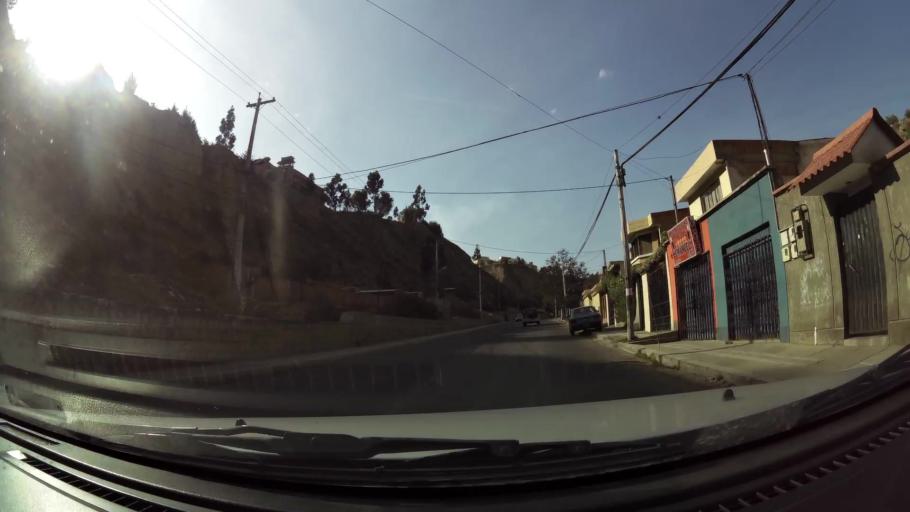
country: BO
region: La Paz
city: La Paz
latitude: -16.5359
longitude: -68.0807
